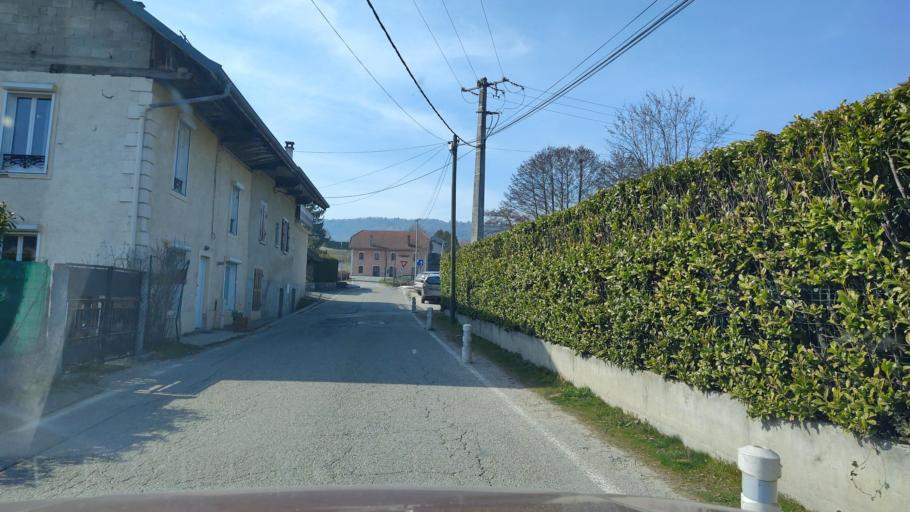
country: FR
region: Rhone-Alpes
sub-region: Departement de la Savoie
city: Albens
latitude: 45.7835
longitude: 5.9469
